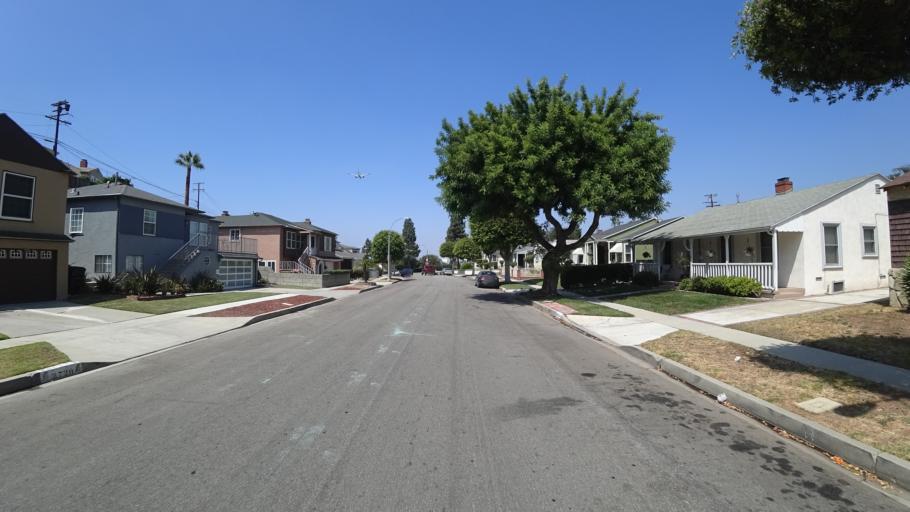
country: US
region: California
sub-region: Los Angeles County
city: Westmont
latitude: 33.9445
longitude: -118.3240
